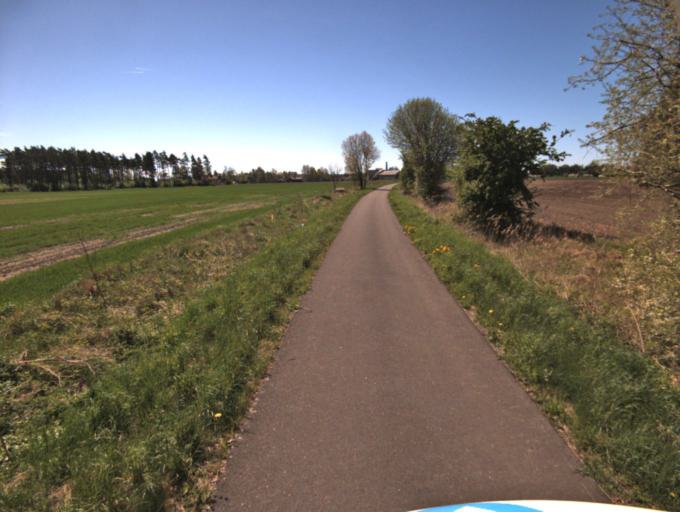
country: SE
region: Skane
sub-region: Kristianstads Kommun
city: Norra Asum
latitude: 55.9548
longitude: 14.1571
